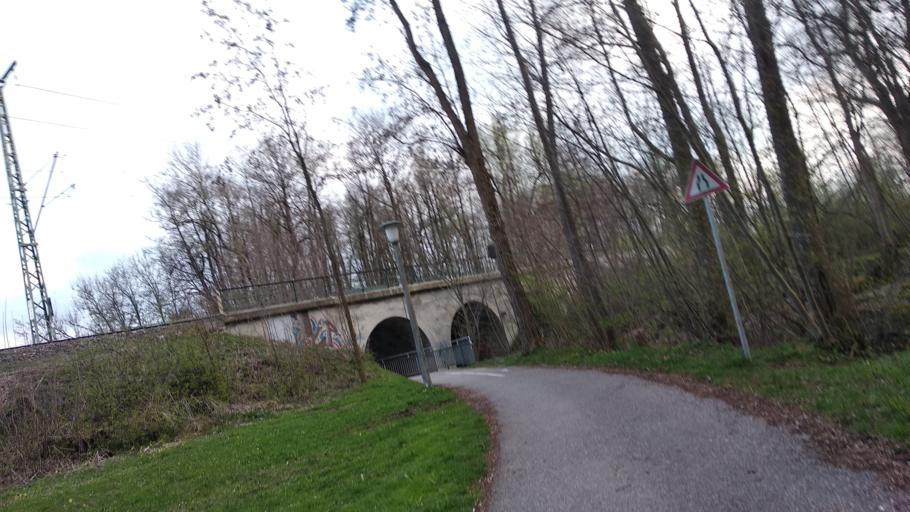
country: DE
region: Bavaria
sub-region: Swabia
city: Mindelheim
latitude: 48.0340
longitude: 10.4902
